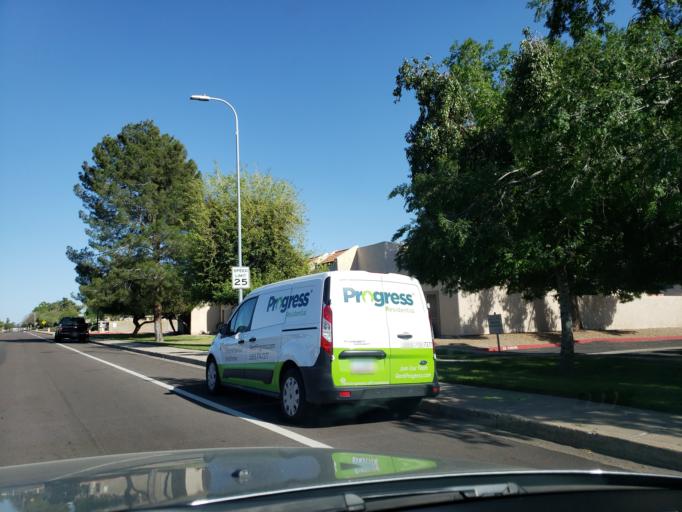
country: US
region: Arizona
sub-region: Maricopa County
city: Glendale
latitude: 33.5603
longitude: -112.1761
